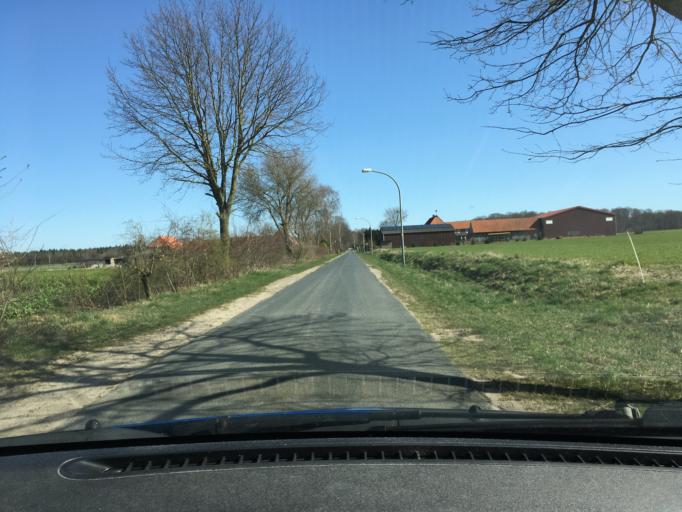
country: DE
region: Lower Saxony
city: Ebstorf
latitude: 53.0254
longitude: 10.4356
